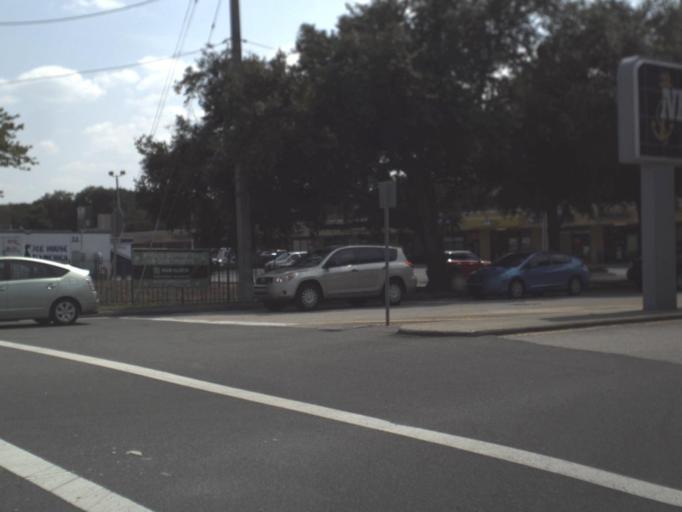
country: US
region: Florida
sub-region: Duval County
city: Atlantic Beach
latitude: 30.3505
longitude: -81.4137
